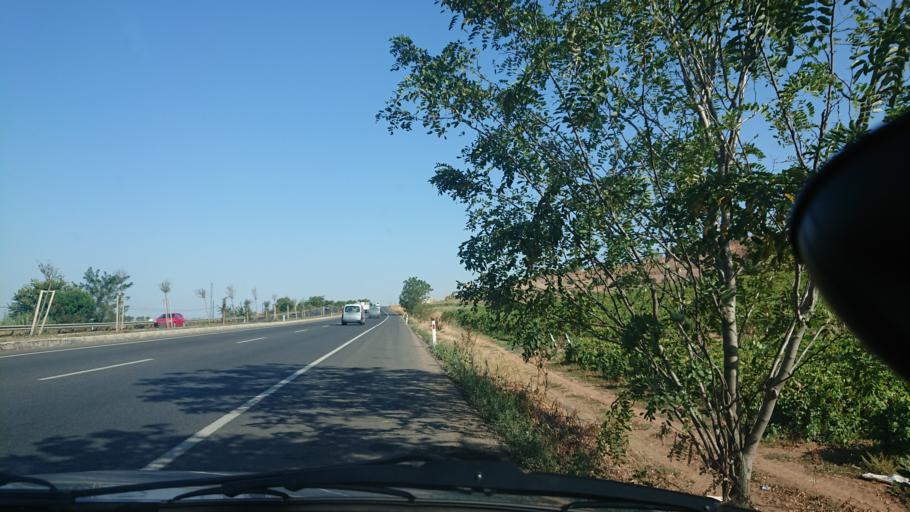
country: TR
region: Manisa
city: Ahmetli
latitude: 38.5105
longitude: 27.9733
